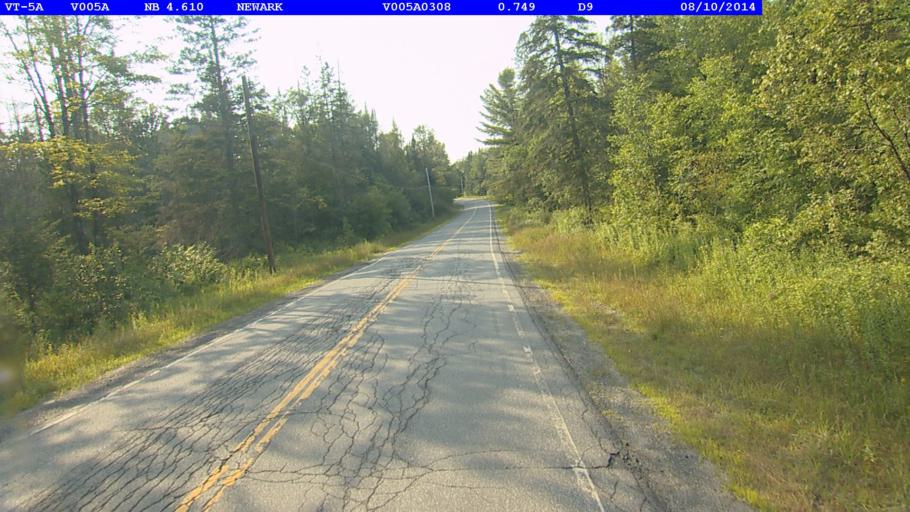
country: US
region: Vermont
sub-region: Caledonia County
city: Lyndonville
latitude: 44.7022
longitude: -72.0058
